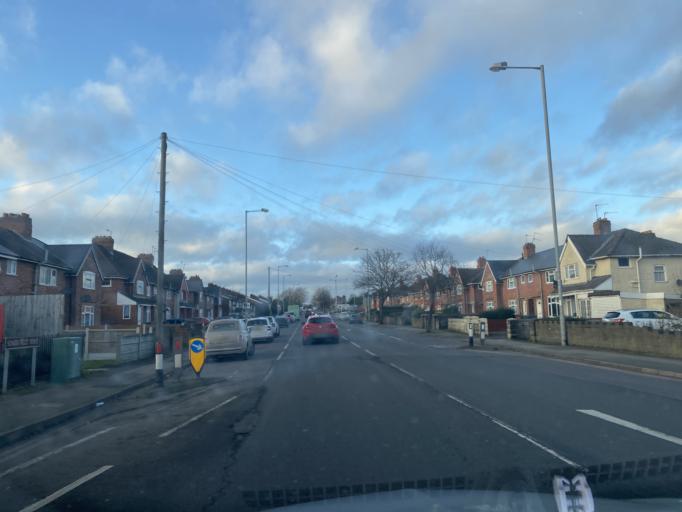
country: GB
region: England
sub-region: Walsall
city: Bloxwich
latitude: 52.6072
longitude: -1.9994
